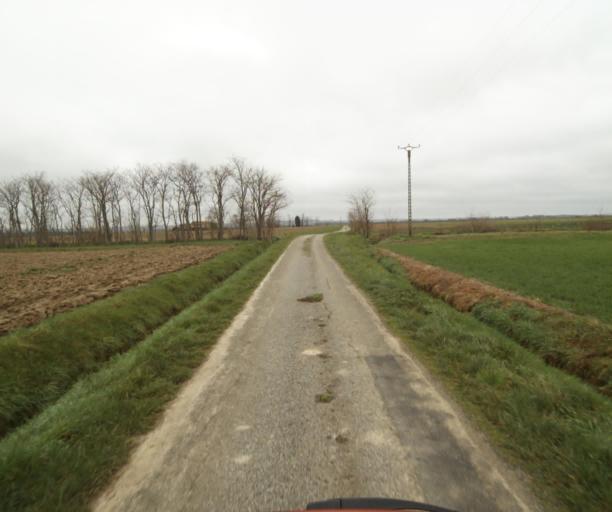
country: FR
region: Midi-Pyrenees
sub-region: Departement de la Haute-Garonne
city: Cintegabelle
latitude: 43.2687
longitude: 1.5291
